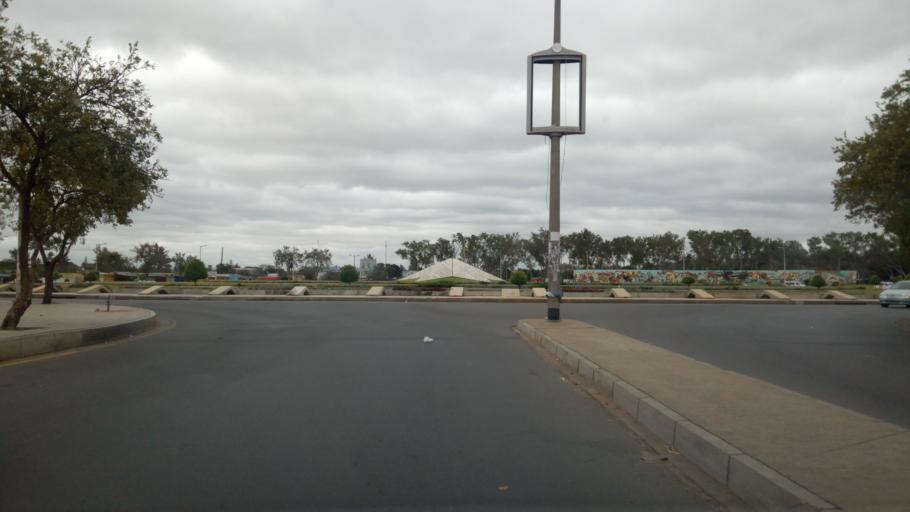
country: MZ
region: Maputo City
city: Maputo
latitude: -25.9347
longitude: 32.5794
